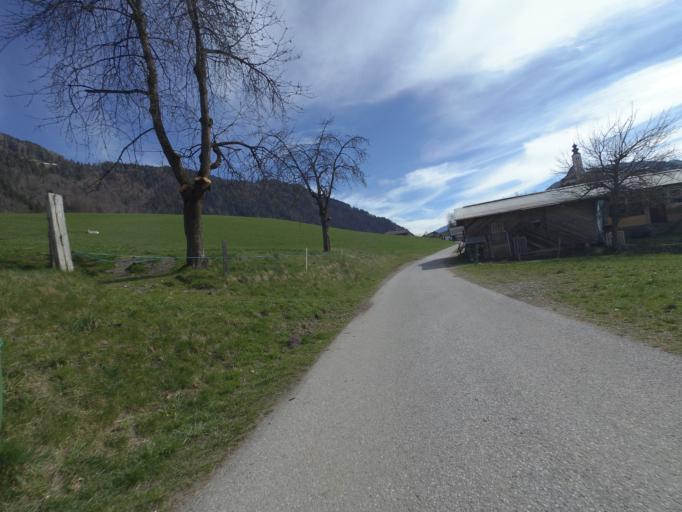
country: AT
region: Salzburg
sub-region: Politischer Bezirk Sankt Johann im Pongau
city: Sankt Veit im Pongau
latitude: 47.3299
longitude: 13.1472
